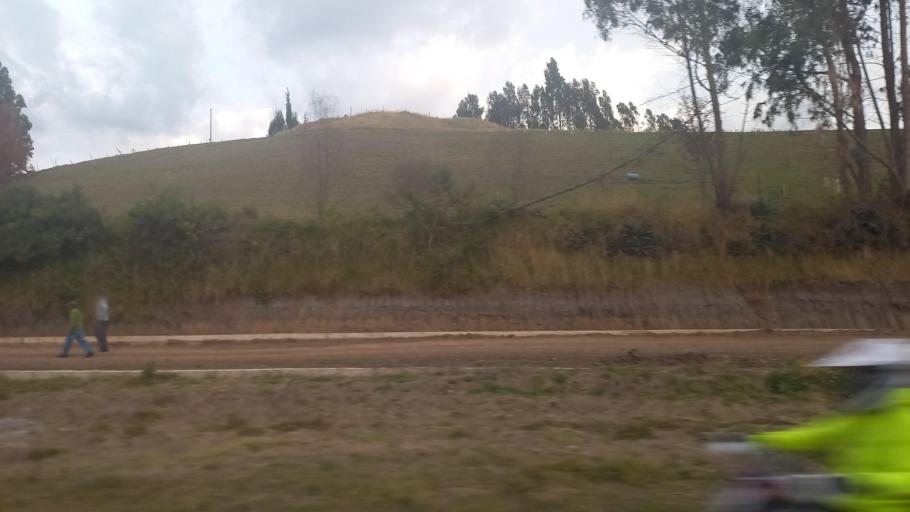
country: EC
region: Pichincha
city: Cayambe
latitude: 0.0871
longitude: -78.1018
